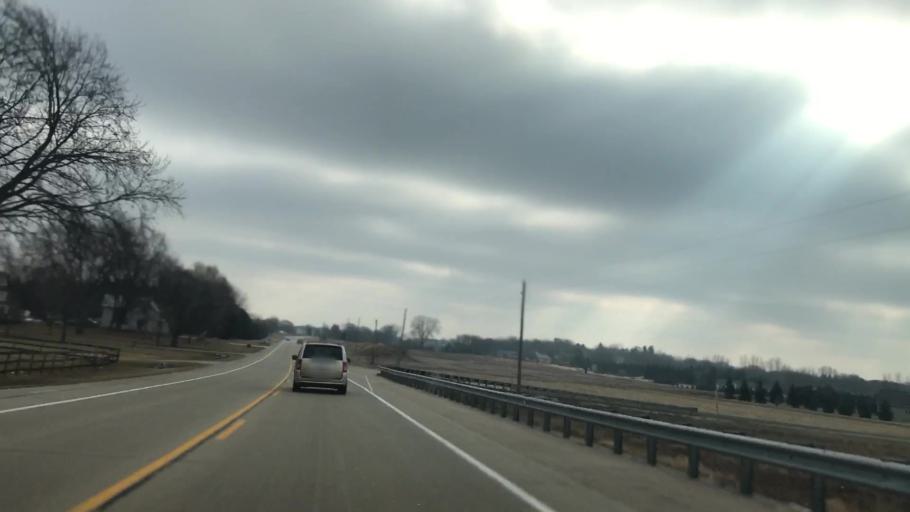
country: US
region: Wisconsin
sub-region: Dodge County
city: Beaver Dam
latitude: 43.4735
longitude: -88.7776
